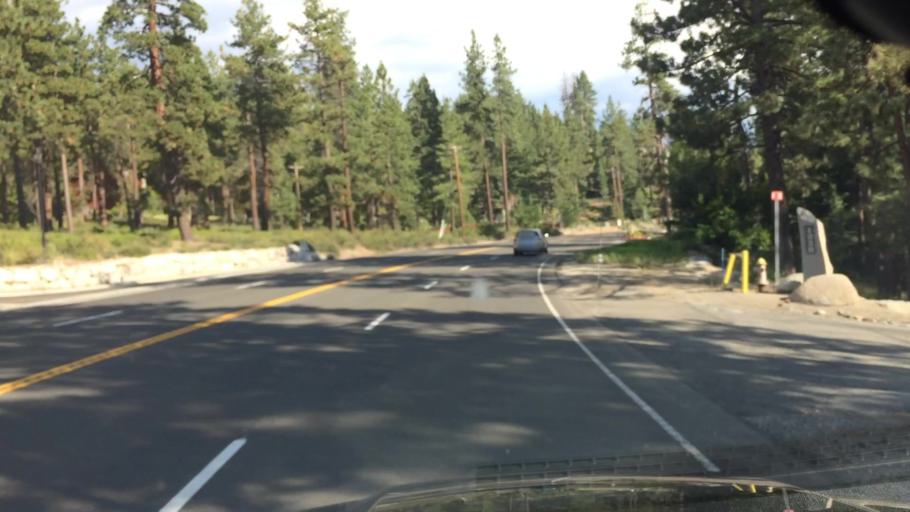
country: US
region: Nevada
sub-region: Douglas County
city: Kingsbury
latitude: 39.0345
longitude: -119.9474
